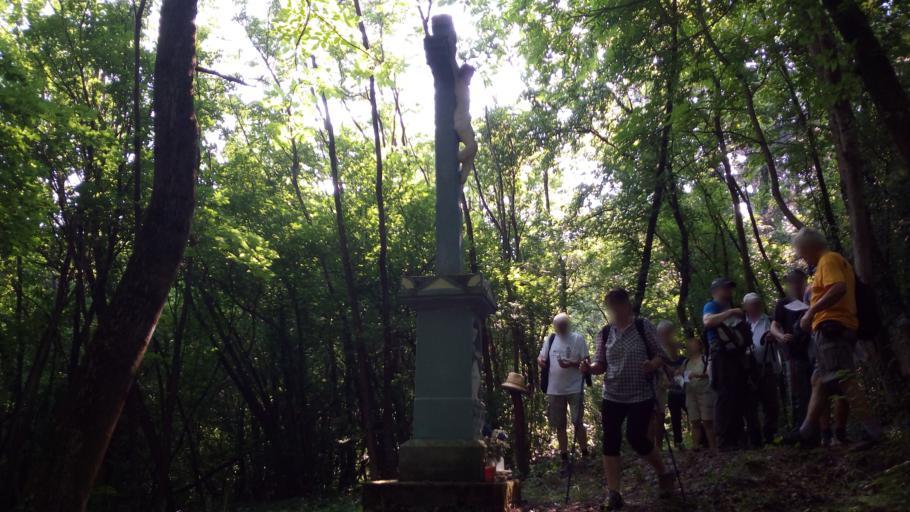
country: HU
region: Baranya
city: Boly
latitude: 46.0190
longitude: 18.4689
